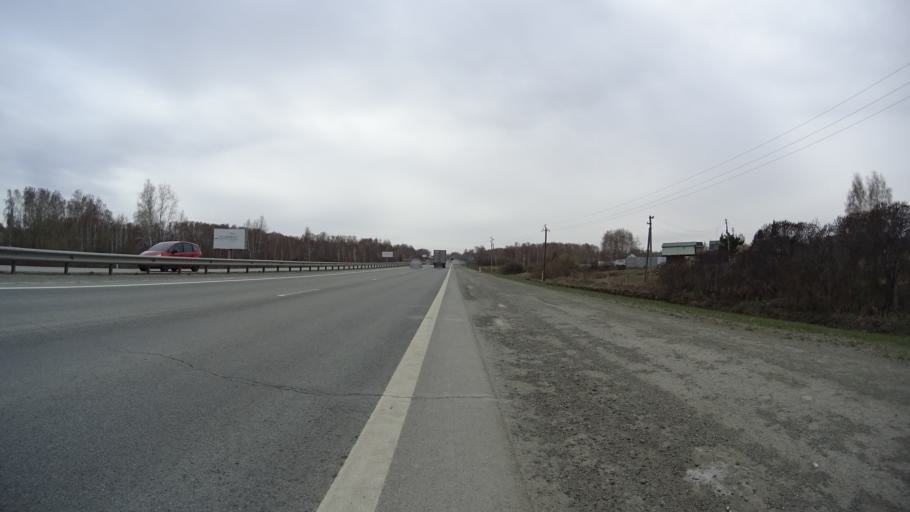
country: RU
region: Chelyabinsk
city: Novosineglazovskiy
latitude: 54.9778
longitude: 61.4111
